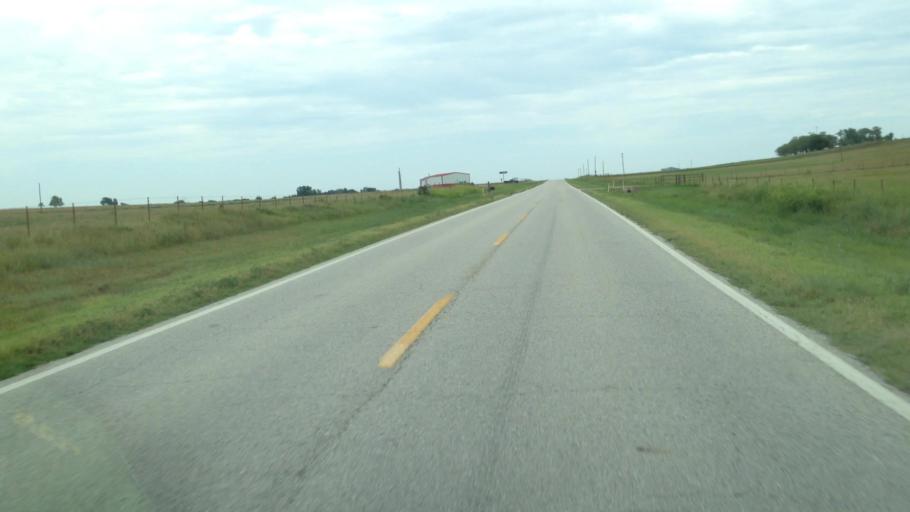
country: US
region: Oklahoma
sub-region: Craig County
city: Vinita
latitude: 36.8273
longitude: -95.1389
